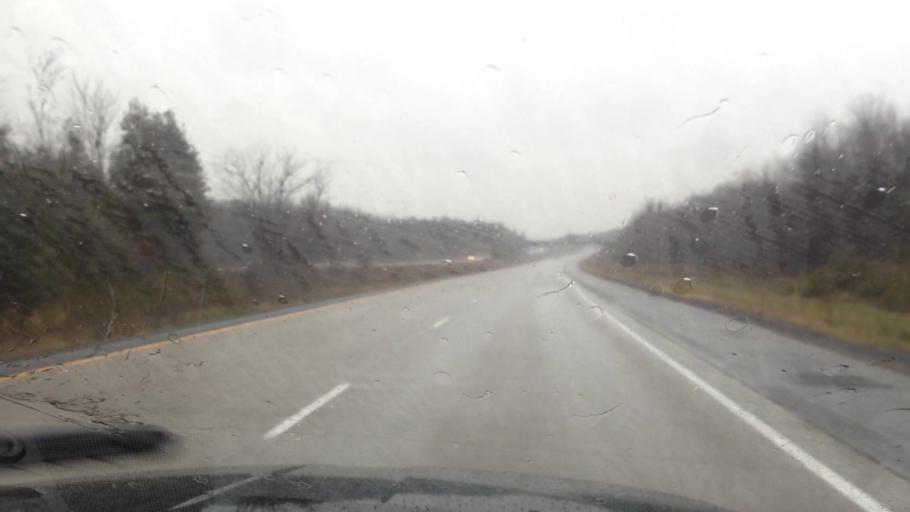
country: CA
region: Ontario
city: Hawkesbury
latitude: 45.4923
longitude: -74.6193
